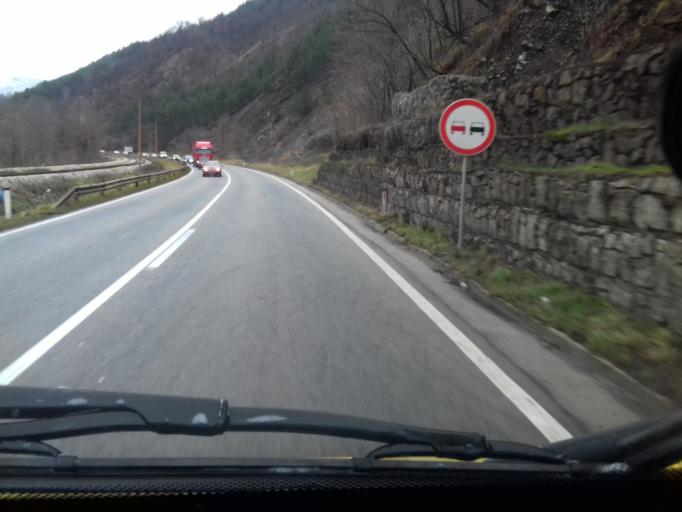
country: BA
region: Federation of Bosnia and Herzegovina
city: Zepce
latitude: 44.4150
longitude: 17.9958
